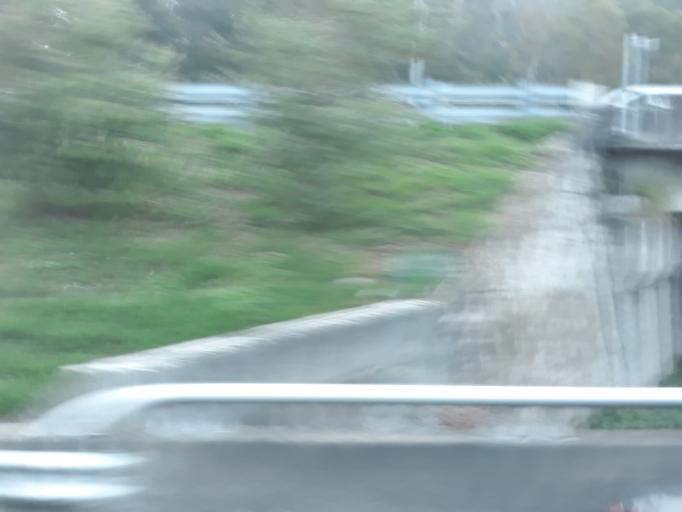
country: TW
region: Taiwan
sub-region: Miaoli
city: Miaoli
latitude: 24.4511
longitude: 120.7826
